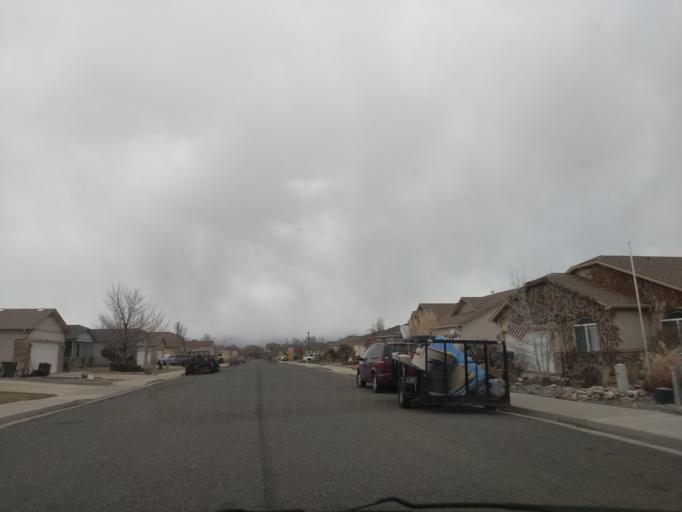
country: US
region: Colorado
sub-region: Mesa County
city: Fruitvale
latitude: 39.0882
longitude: -108.5234
